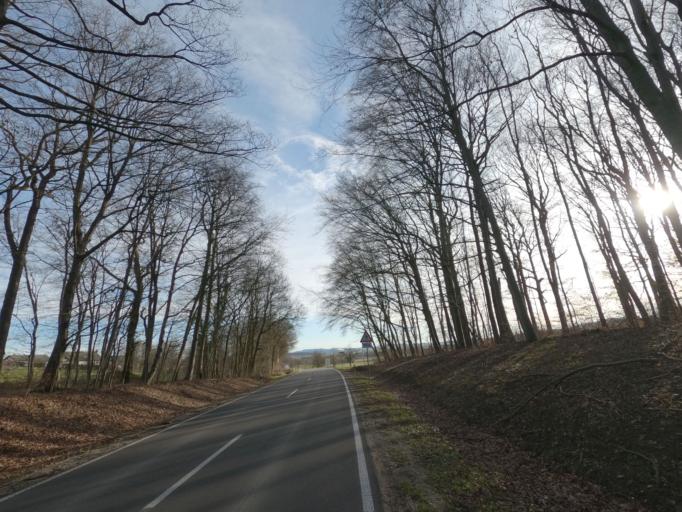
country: DE
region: Baden-Wuerttemberg
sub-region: Regierungsbezirk Stuttgart
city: Hattenhofen
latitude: 48.6690
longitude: 9.6001
